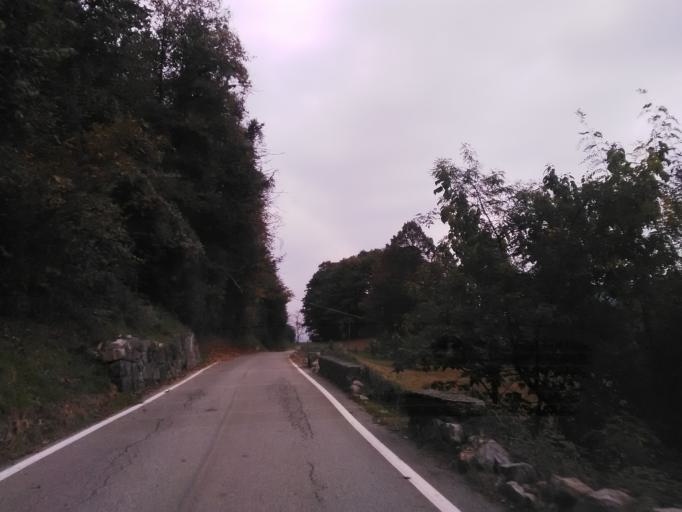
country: IT
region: Piedmont
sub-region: Provincia di Vercelli
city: Quarona
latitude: 45.7464
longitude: 8.2560
